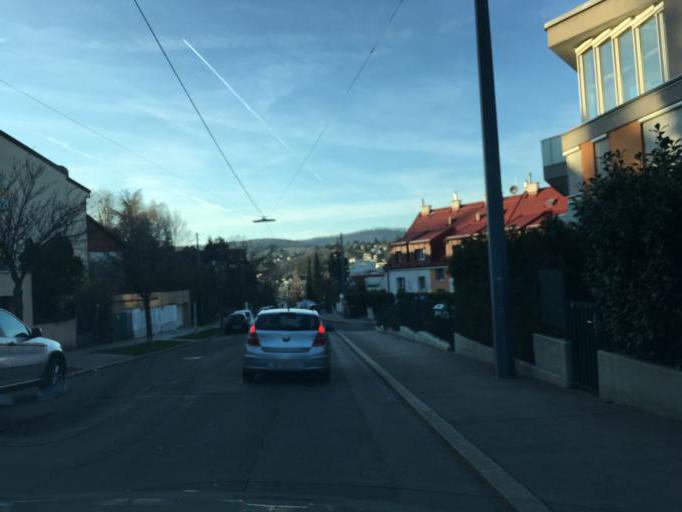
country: AT
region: Vienna
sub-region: Wien Stadt
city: Vienna
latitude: 48.2410
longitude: 16.3245
